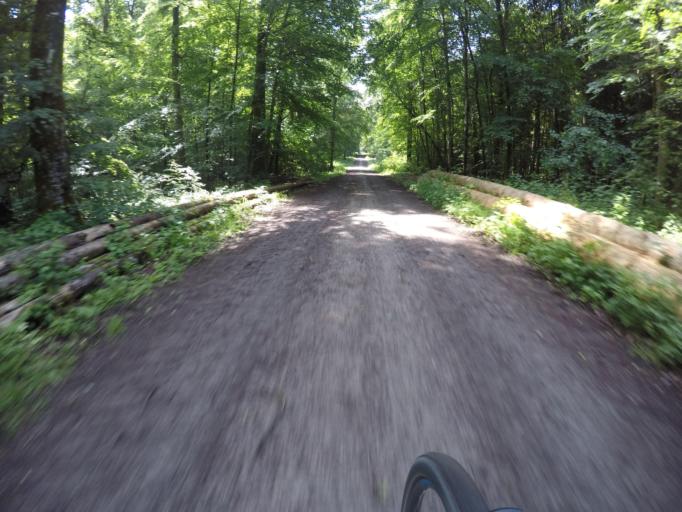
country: DE
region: Baden-Wuerttemberg
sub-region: Regierungsbezirk Stuttgart
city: Nufringen
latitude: 48.6358
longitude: 8.8592
